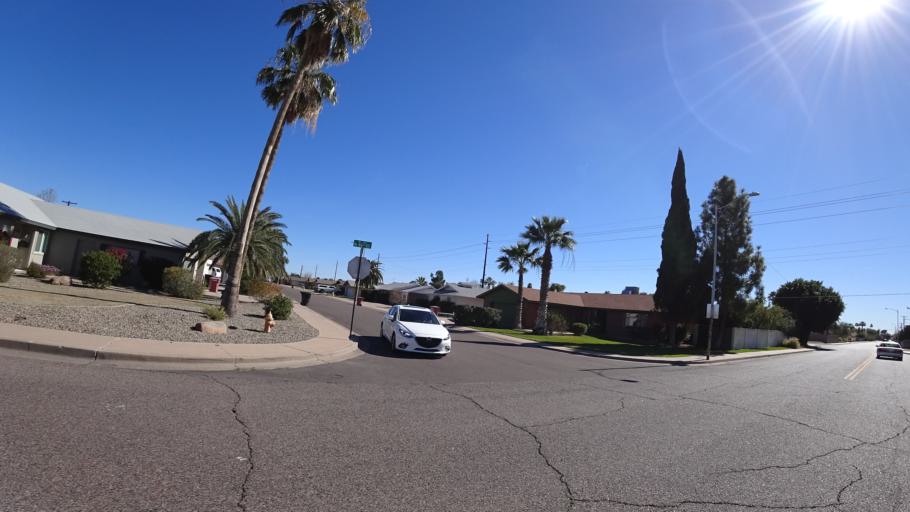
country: US
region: Arizona
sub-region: Maricopa County
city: Scottsdale
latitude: 33.5139
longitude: -111.8960
